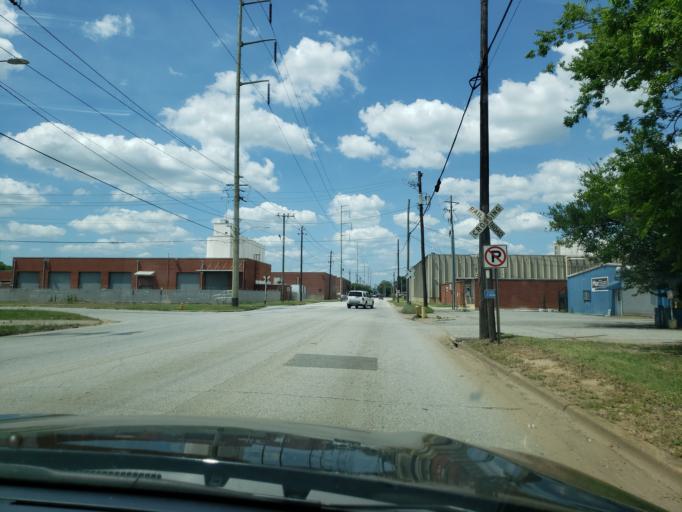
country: US
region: Georgia
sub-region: Muscogee County
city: Columbus
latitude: 32.4549
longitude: -84.9798
